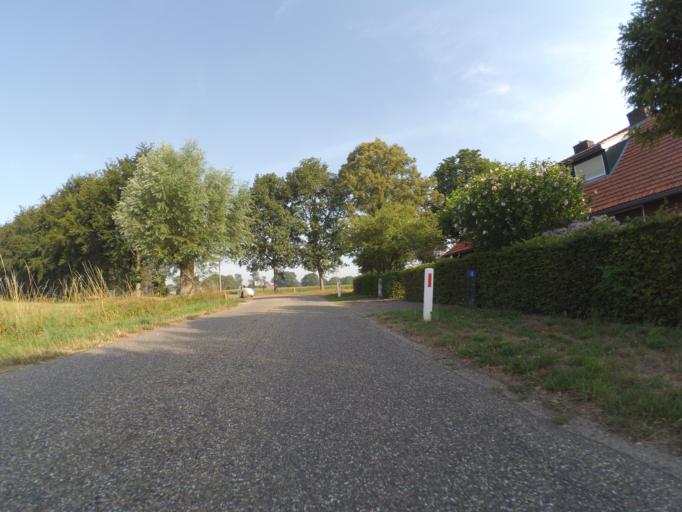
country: NL
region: Overijssel
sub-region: Gemeente Wierden
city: Wierden
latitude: 52.3221
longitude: 6.6152
